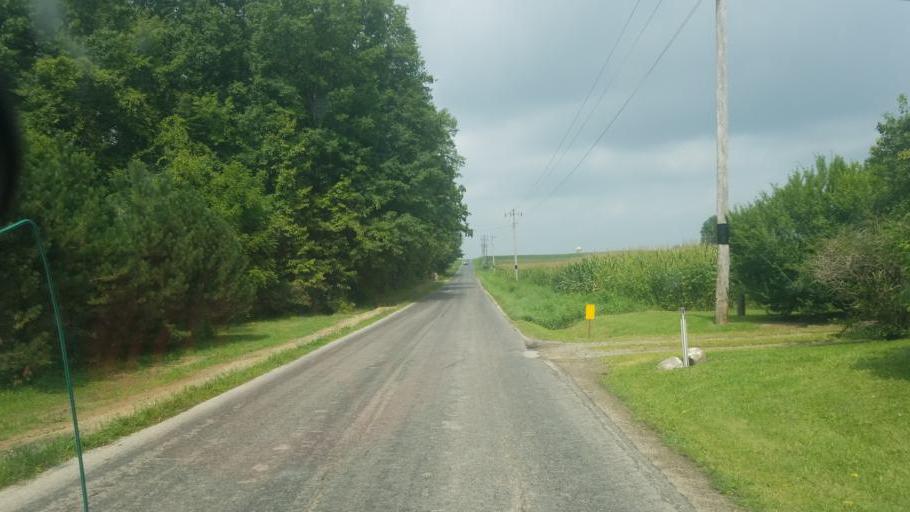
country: US
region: Ohio
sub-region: Huron County
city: Greenwich
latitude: 40.9903
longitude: -82.4783
